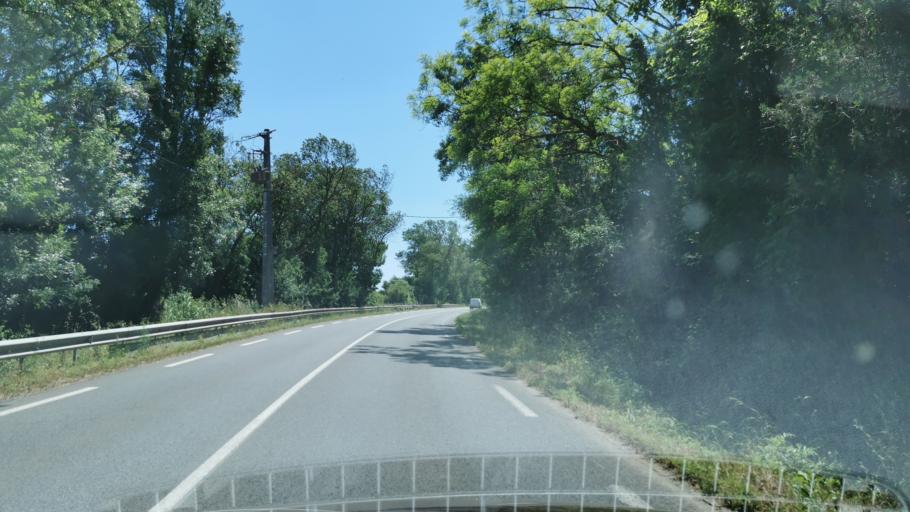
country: FR
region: Languedoc-Roussillon
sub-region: Departement de l'Aude
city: Narbonne
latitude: 43.2183
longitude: 3.0112
